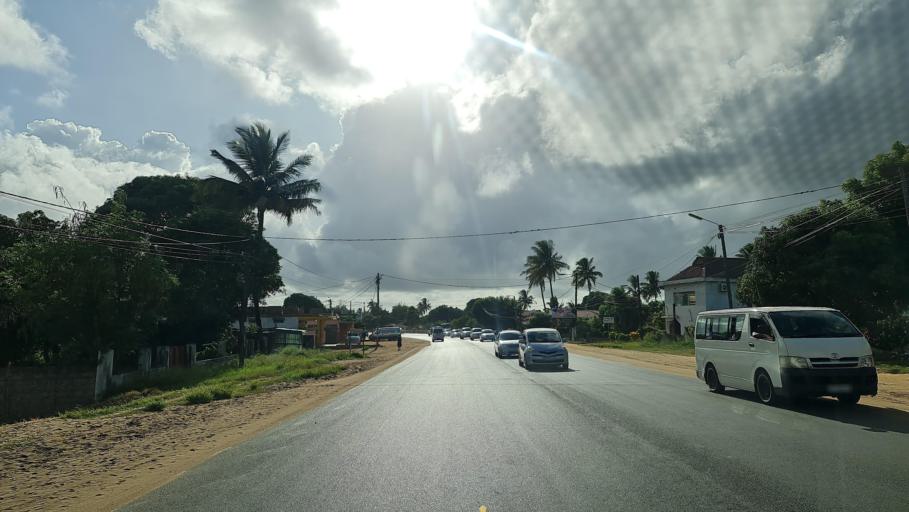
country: MZ
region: Gaza
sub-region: Xai-Xai District
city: Xai-Xai
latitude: -25.0570
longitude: 33.6622
